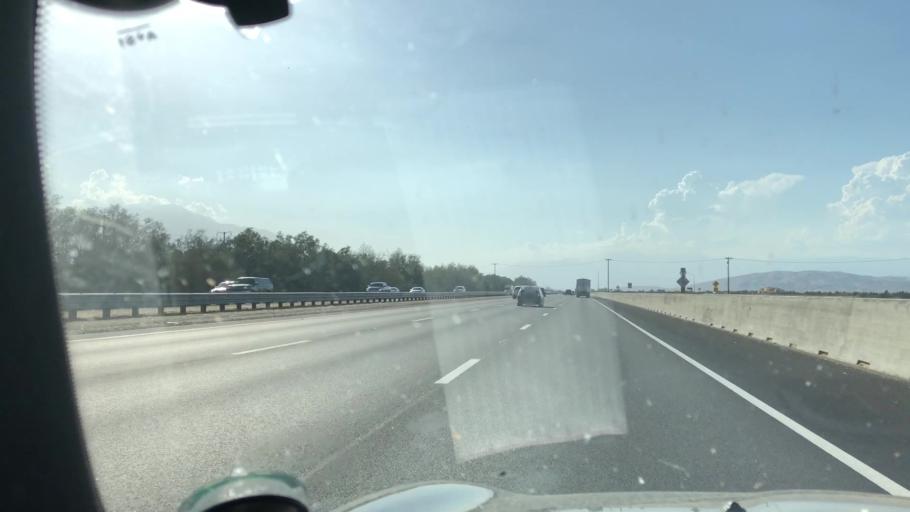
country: US
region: California
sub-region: Riverside County
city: Bermuda Dunes
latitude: 33.7709
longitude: -116.3289
